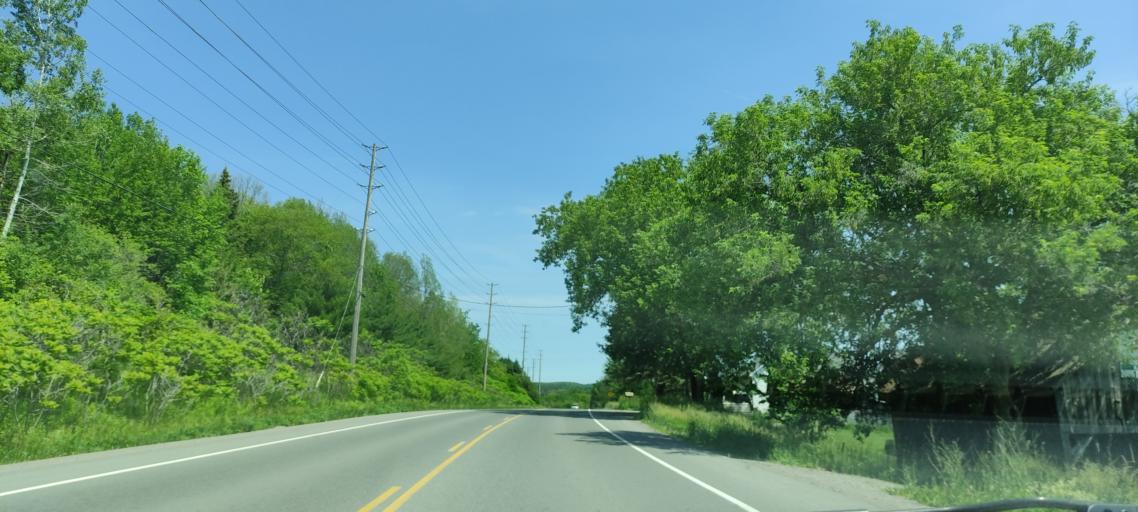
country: CA
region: Ontario
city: Quinte West
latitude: 44.2415
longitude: -77.8183
